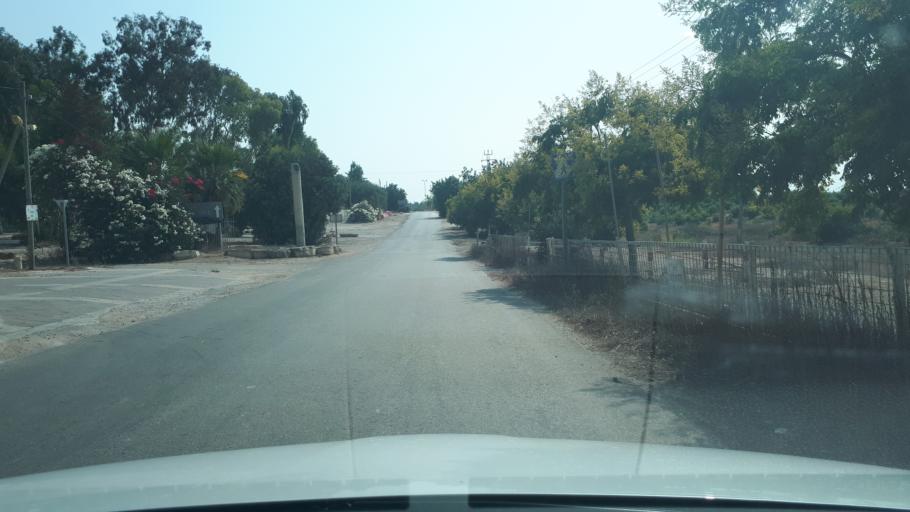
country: IL
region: Central District
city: Rosh Ha'Ayin
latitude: 32.0641
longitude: 34.9465
